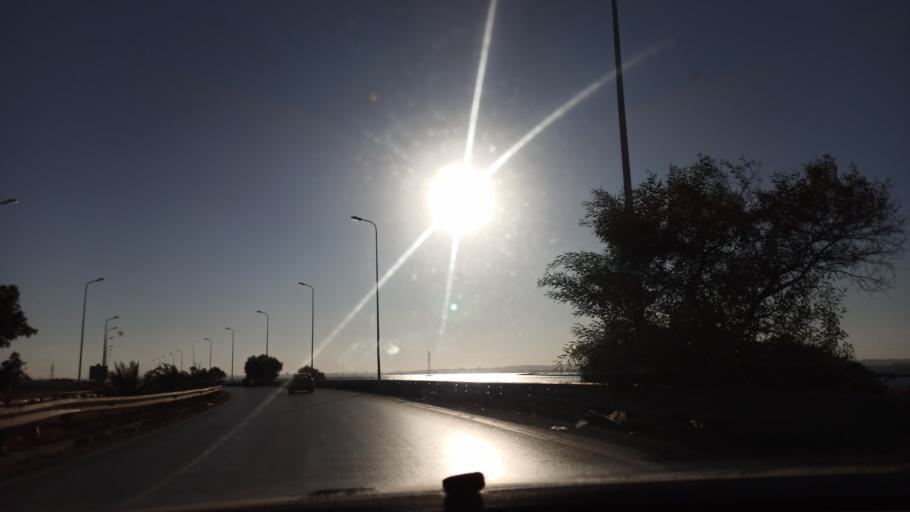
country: TN
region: Tunis
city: La Goulette
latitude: 36.8246
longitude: 10.3047
